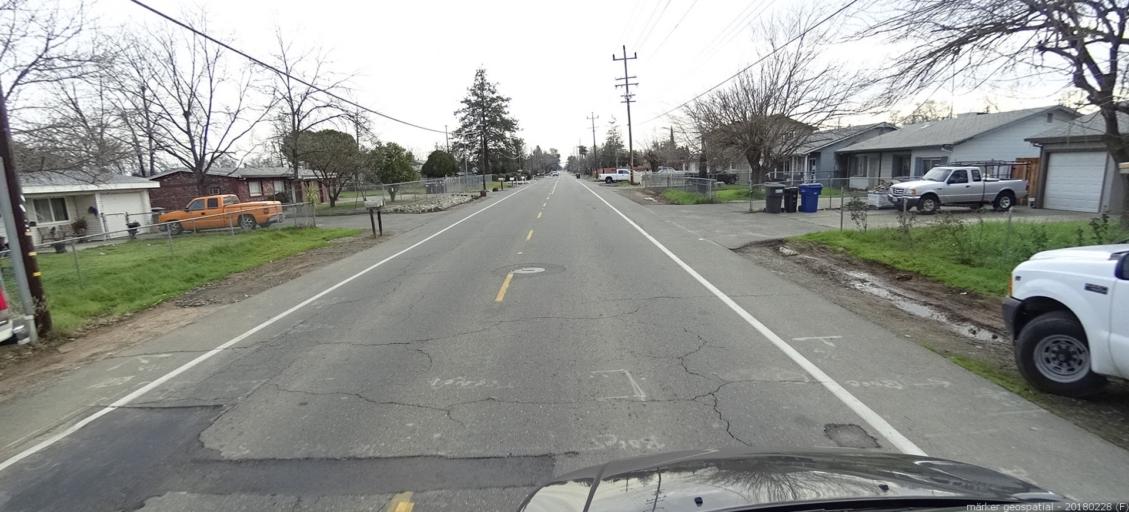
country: US
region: California
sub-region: Sacramento County
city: Rio Linda
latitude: 38.6984
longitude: -121.4513
